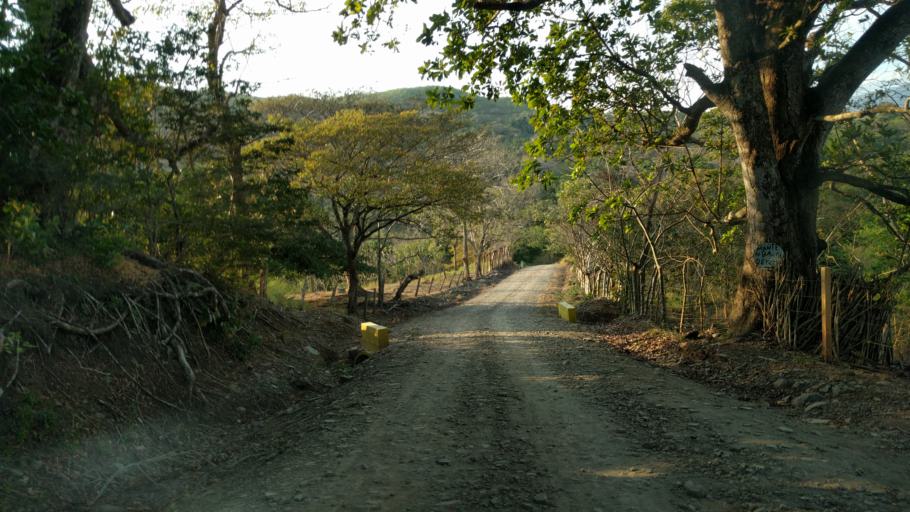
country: CR
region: Puntarenas
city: Esparza
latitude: 10.0172
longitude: -84.6956
